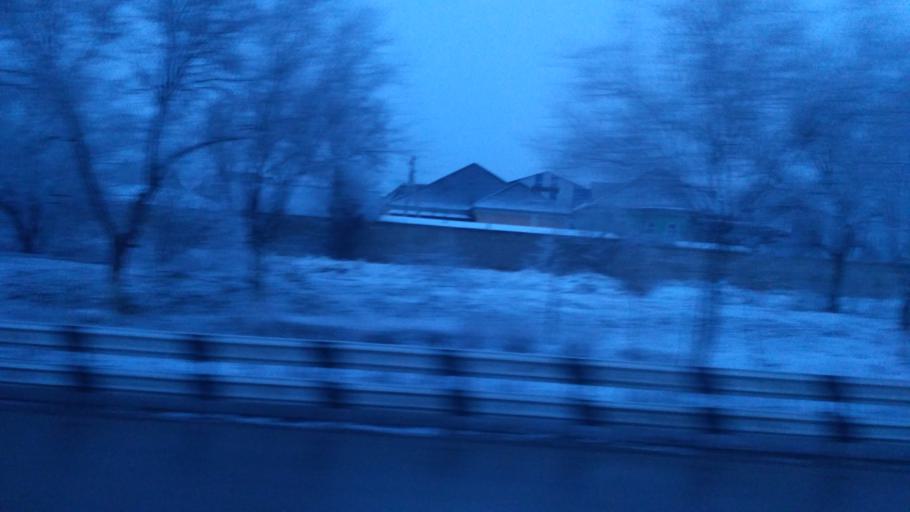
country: KZ
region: Ongtustik Qazaqstan
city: Shymkent
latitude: 42.3563
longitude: 69.5244
